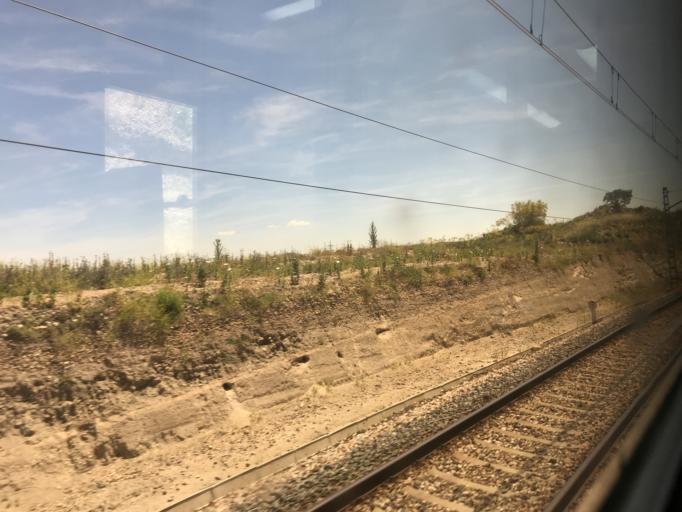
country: ES
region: Madrid
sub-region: Provincia de Madrid
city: Ciempozuelos
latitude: 40.1837
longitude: -3.6387
